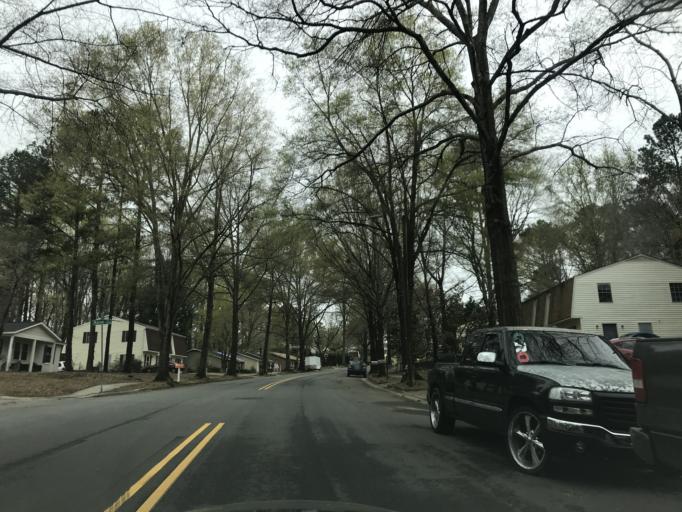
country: US
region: North Carolina
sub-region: Wake County
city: West Raleigh
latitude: 35.8751
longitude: -78.6491
